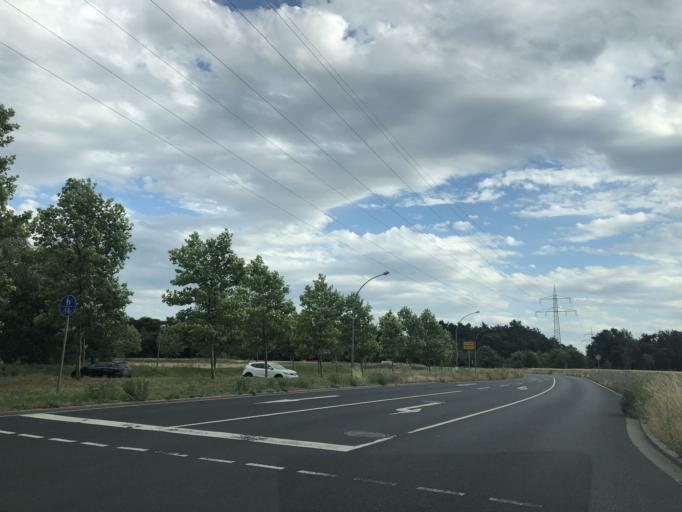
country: DE
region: Hesse
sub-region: Regierungsbezirk Darmstadt
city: Dietzenbach
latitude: 50.0166
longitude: 8.8052
